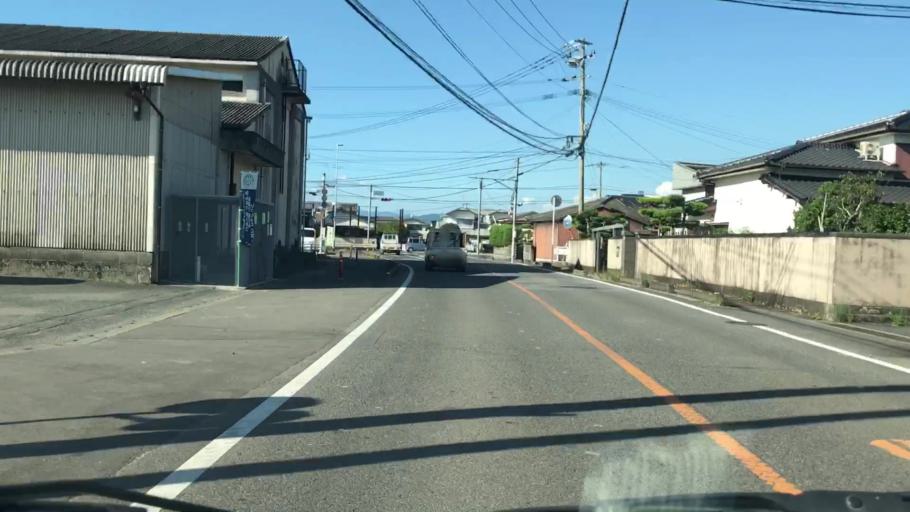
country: JP
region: Saga Prefecture
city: Saga-shi
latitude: 33.2180
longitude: 130.2638
